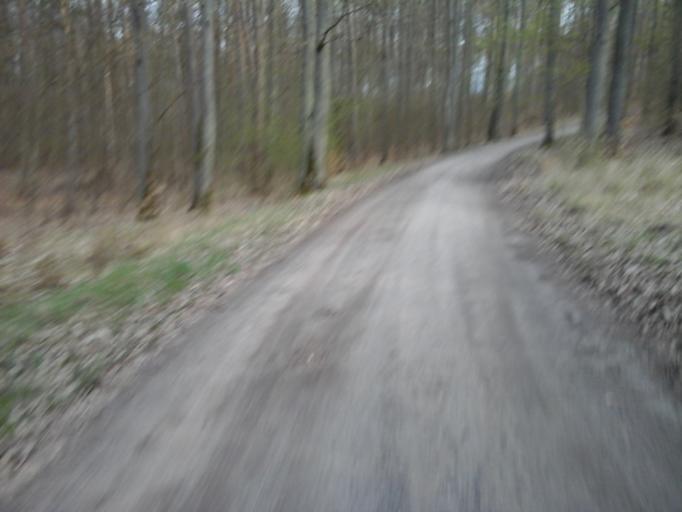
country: PL
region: West Pomeranian Voivodeship
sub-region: Powiat choszczenski
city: Bierzwnik
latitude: 53.0470
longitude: 15.5963
